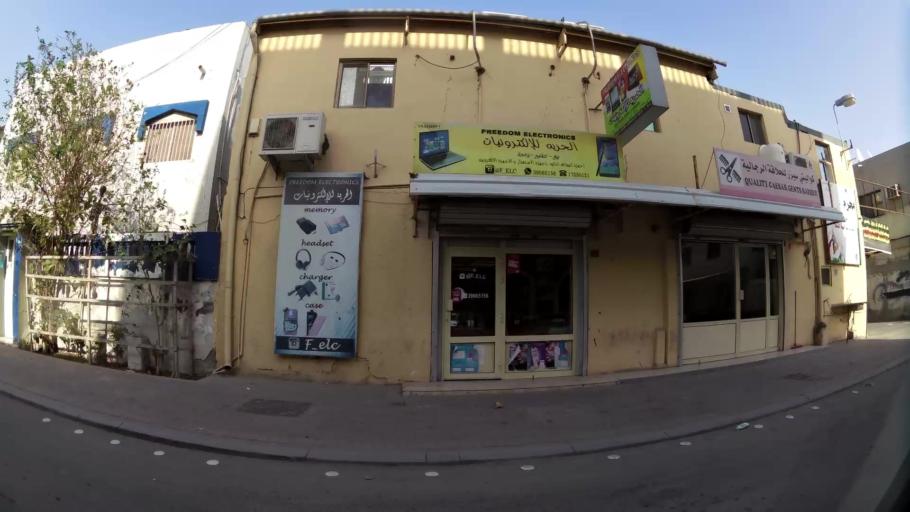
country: BH
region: Manama
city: Jidd Hafs
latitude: 26.2151
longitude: 50.5125
